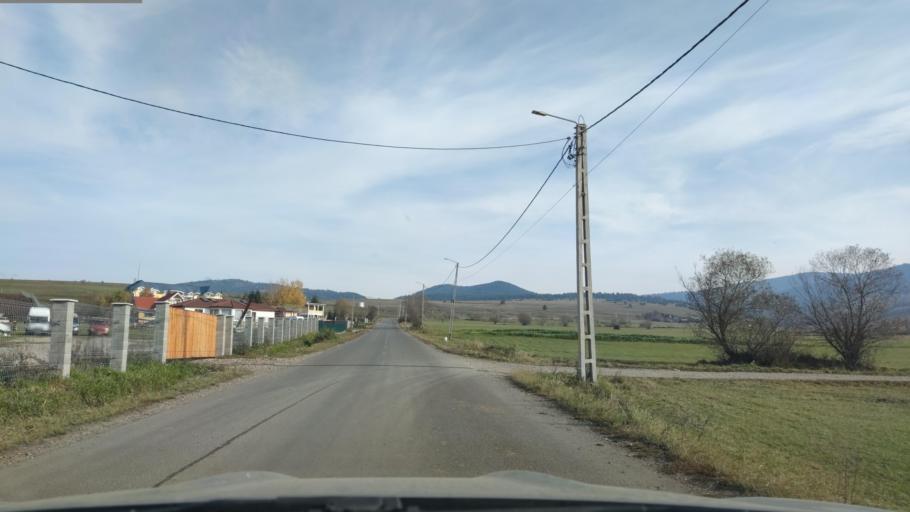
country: RO
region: Harghita
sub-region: Comuna Ditrau
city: Ditrau
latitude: 46.8209
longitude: 25.5297
